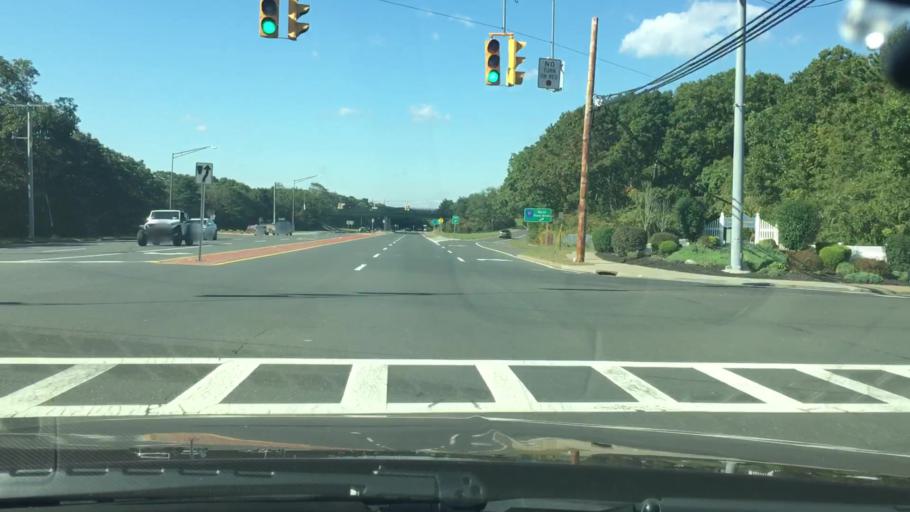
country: US
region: New York
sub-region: Suffolk County
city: Holtsville
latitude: 40.7895
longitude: -73.0489
